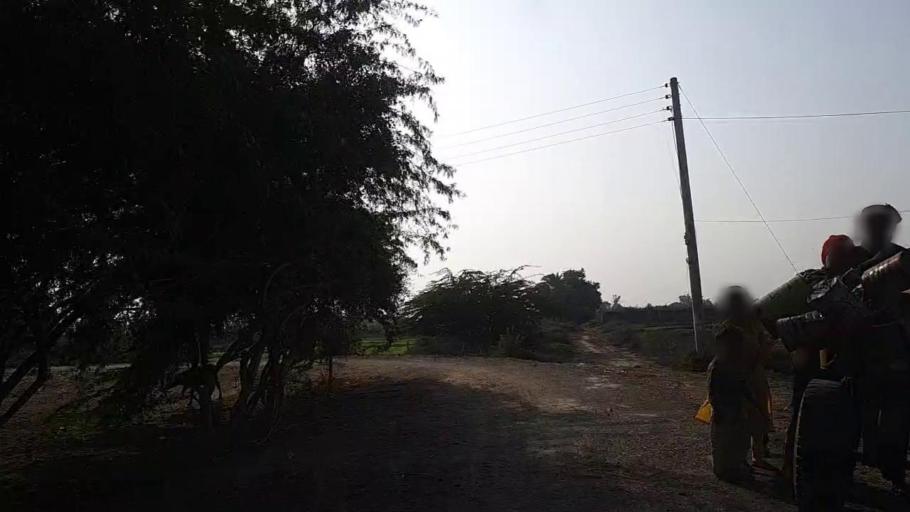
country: PK
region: Sindh
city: Keti Bandar
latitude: 24.1652
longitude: 67.6275
